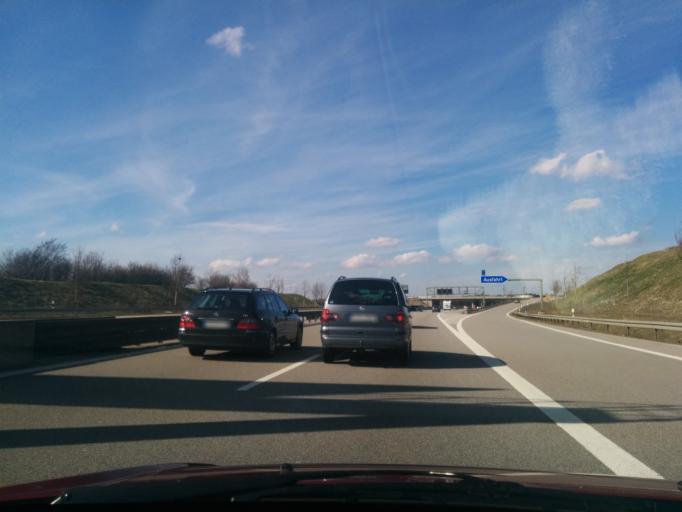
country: DE
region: Bavaria
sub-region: Upper Bavaria
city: Germering
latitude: 48.1427
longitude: 11.3951
